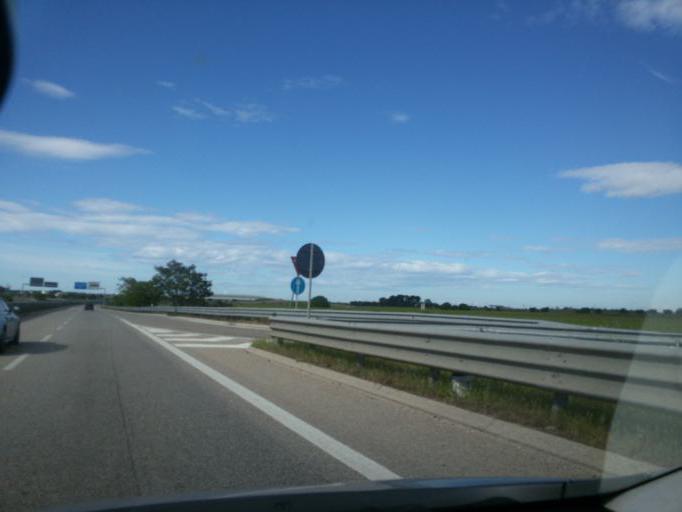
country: IT
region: Apulia
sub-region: Provincia di Brindisi
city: Francavilla Fontana
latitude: 40.5378
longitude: 17.5319
